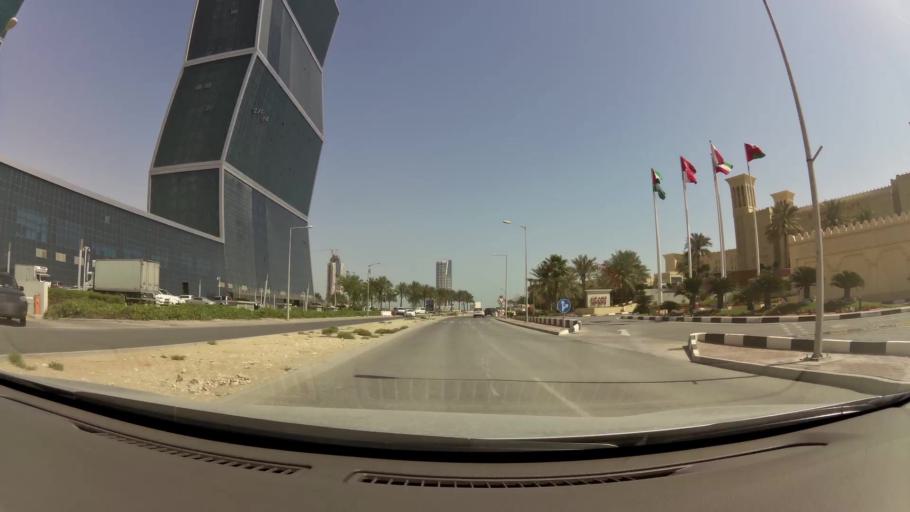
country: QA
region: Baladiyat ad Dawhah
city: Doha
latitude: 25.3768
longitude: 51.5265
